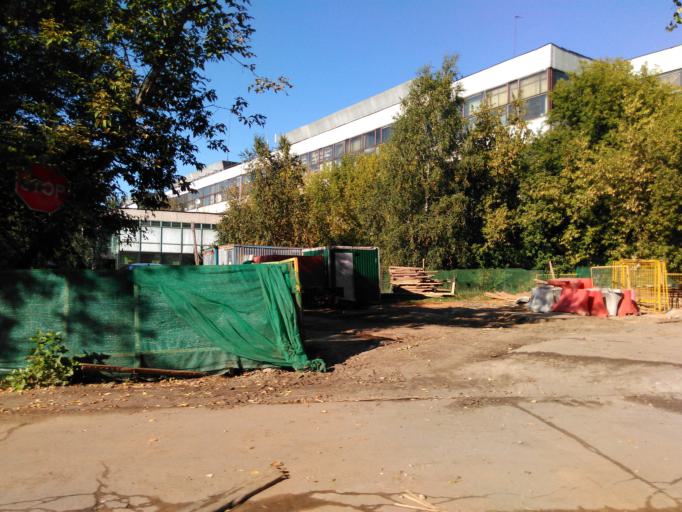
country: RU
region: Moscow
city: Likhobory
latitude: 55.8498
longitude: 37.5679
